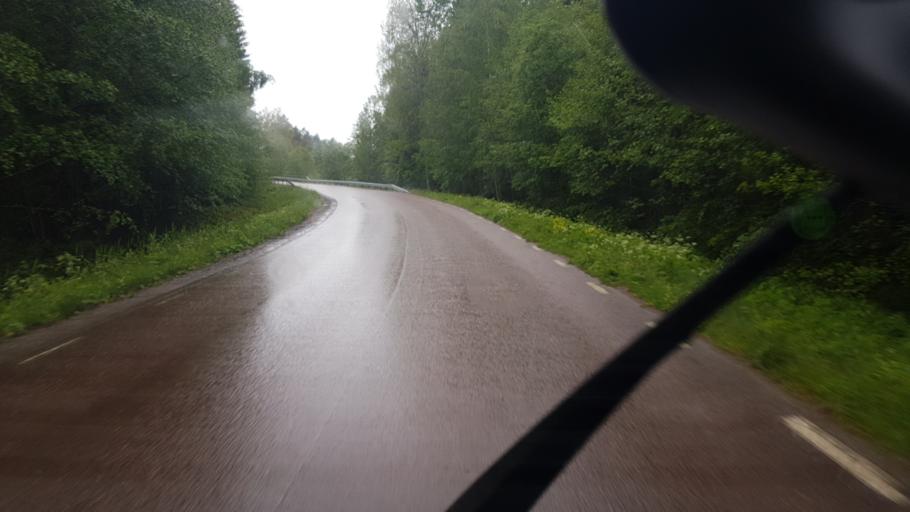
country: SE
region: Vaermland
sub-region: Arvika Kommun
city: Arvika
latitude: 59.7076
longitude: 12.4988
